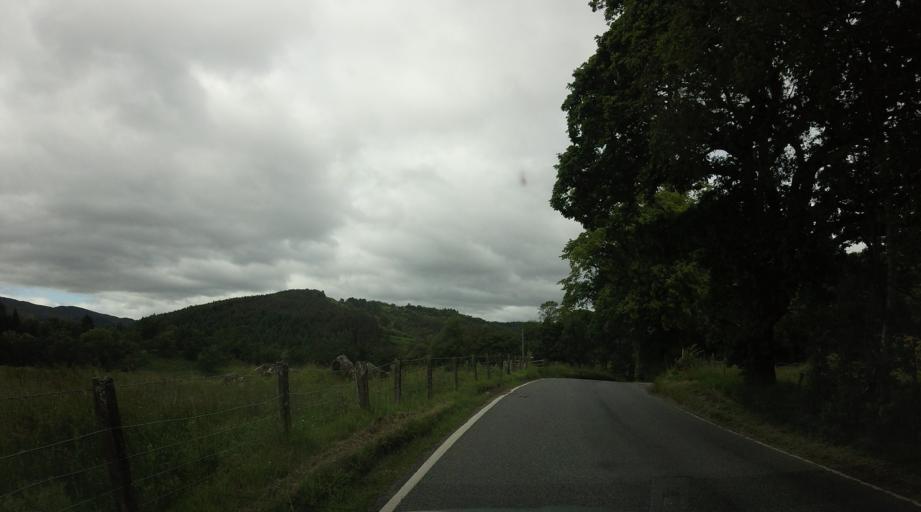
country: GB
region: Scotland
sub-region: Perth and Kinross
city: Pitlochry
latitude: 56.7277
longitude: -3.8188
